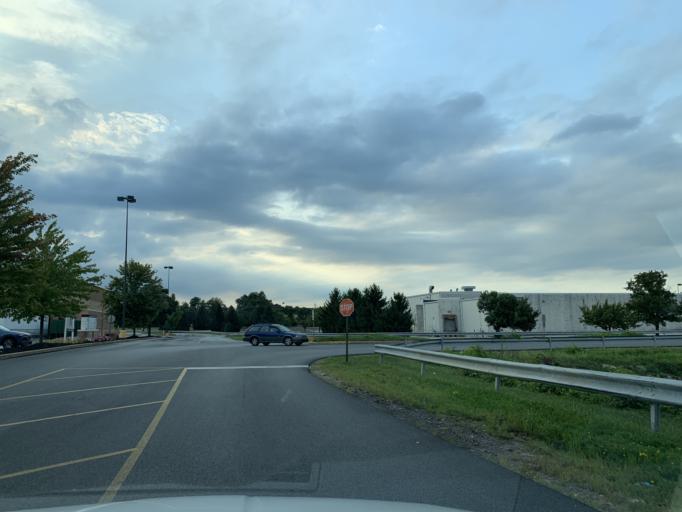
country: US
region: Pennsylvania
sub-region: York County
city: West York
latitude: 39.9725
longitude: -76.7692
